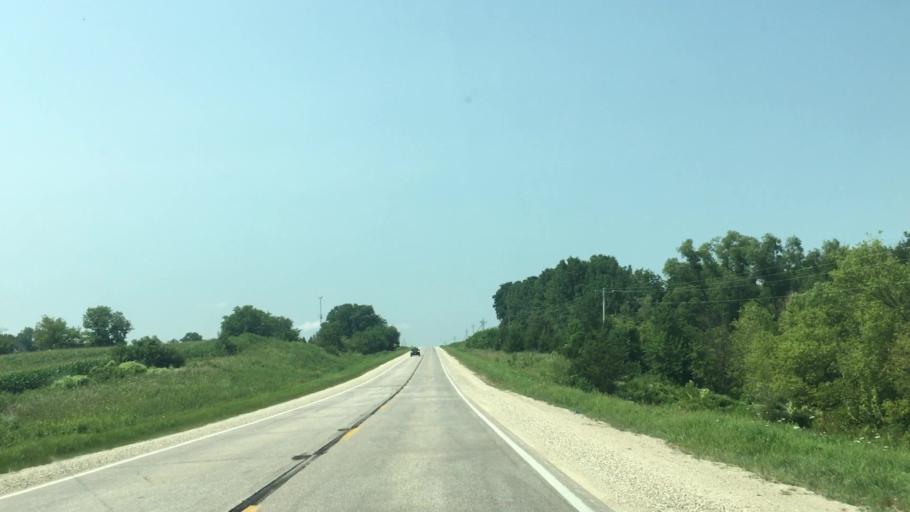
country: US
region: Iowa
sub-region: Fayette County
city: West Union
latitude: 43.0848
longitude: -91.8475
